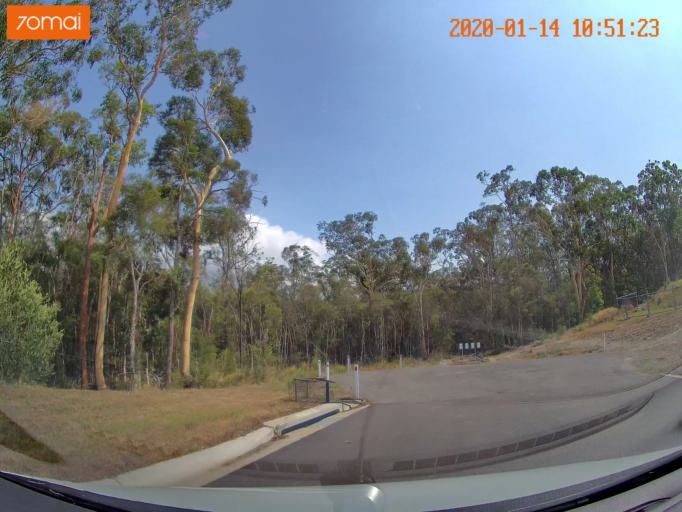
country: AU
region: New South Wales
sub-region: Lake Macquarie Shire
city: Dora Creek
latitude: -33.0984
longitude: 151.4839
